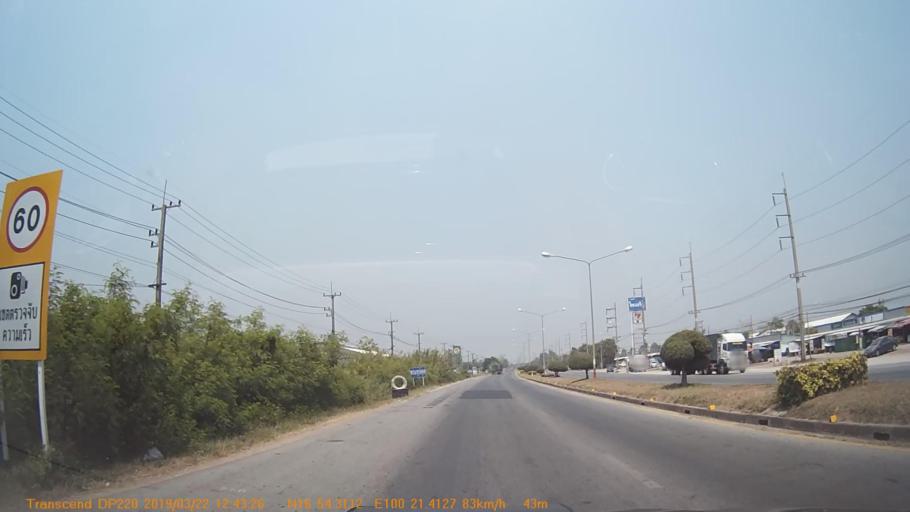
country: TH
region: Phitsanulok
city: Wat Bot
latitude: 16.9056
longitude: 100.3569
